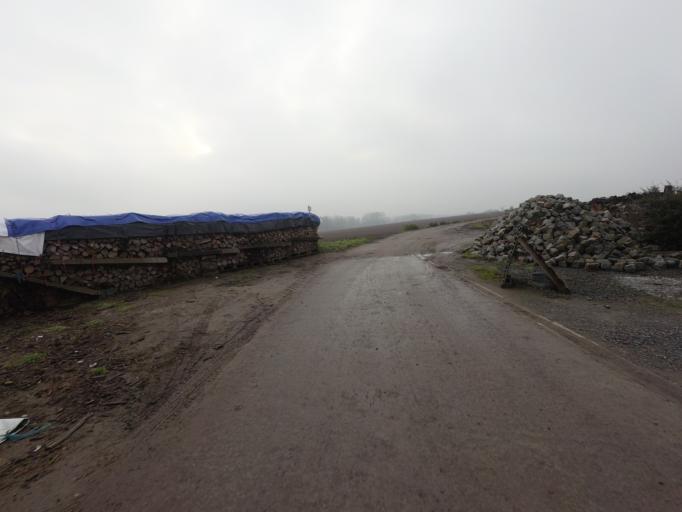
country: BE
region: Flanders
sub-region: Provincie Oost-Vlaanderen
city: Ninove
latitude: 50.8244
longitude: 3.9884
